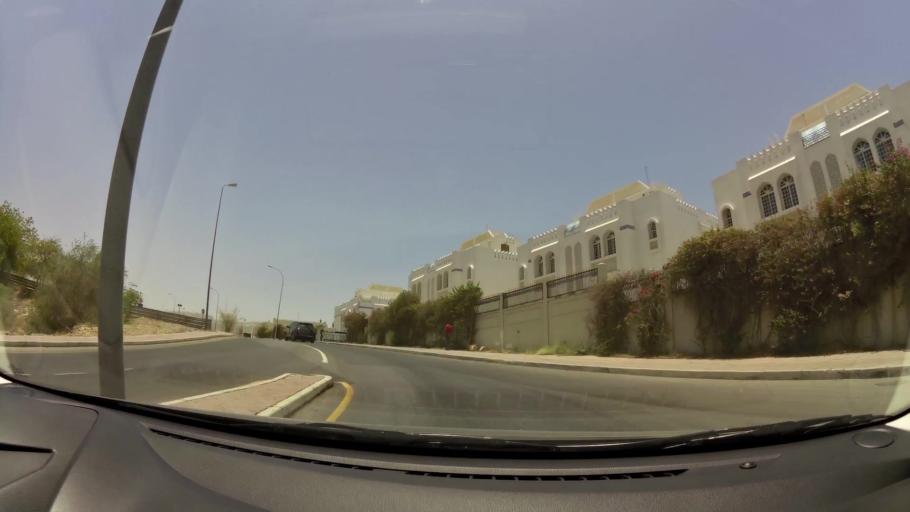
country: OM
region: Muhafazat Masqat
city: Bawshar
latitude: 23.6067
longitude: 58.4887
